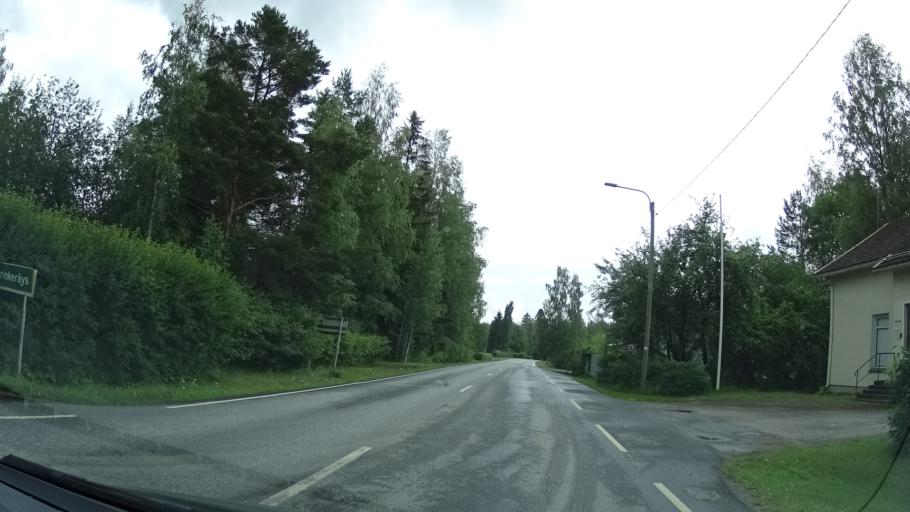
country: FI
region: Pirkanmaa
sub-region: Lounais-Pirkanmaa
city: Punkalaidun
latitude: 61.1018
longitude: 23.2844
